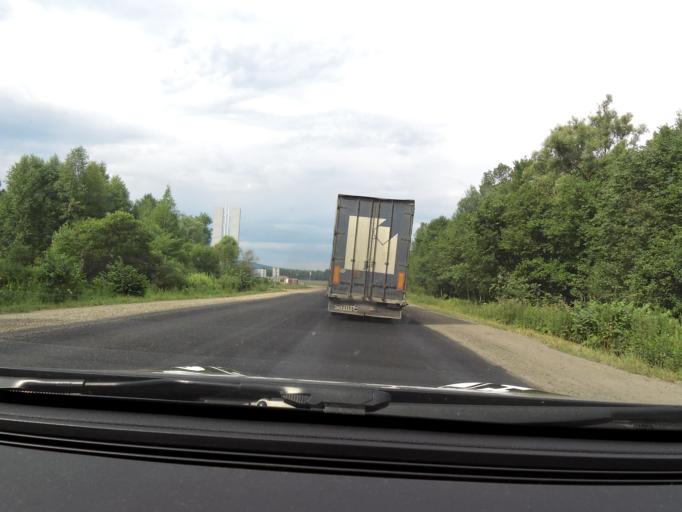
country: RU
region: Bashkortostan
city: Ulu-Telyak
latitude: 54.8566
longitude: 57.1415
